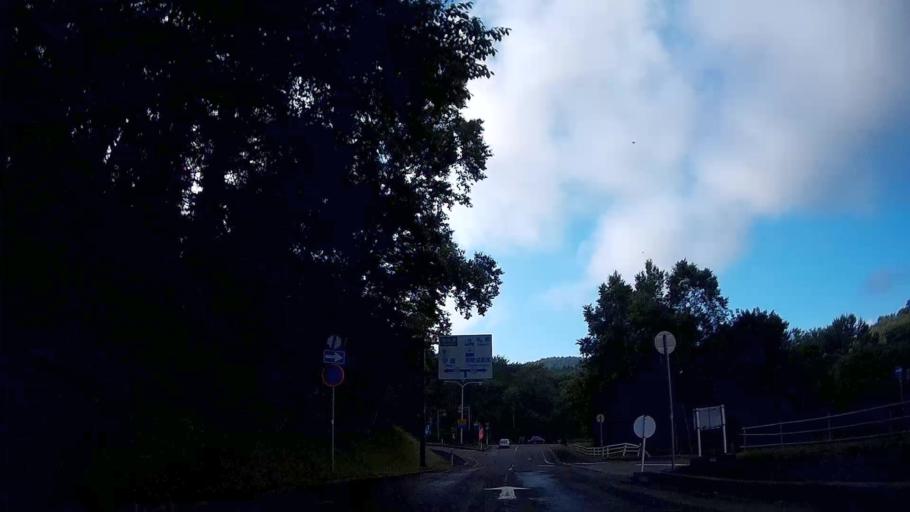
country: JP
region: Hokkaido
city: Date
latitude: 42.5417
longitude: 140.8574
